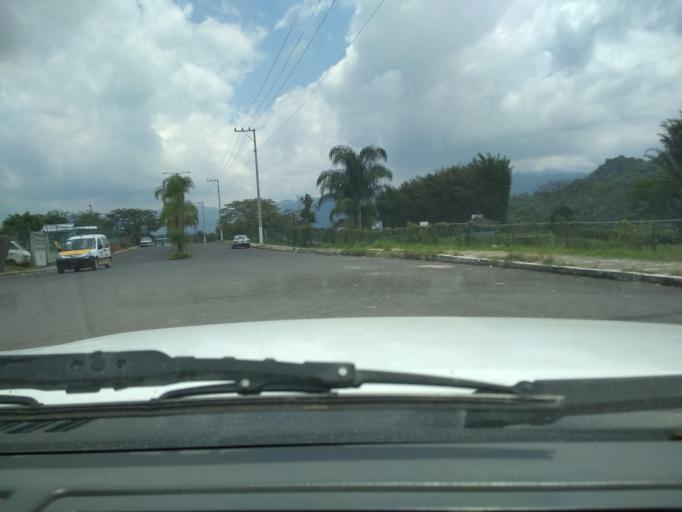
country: MX
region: Veracruz
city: Cordoba
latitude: 18.8889
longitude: -96.9203
